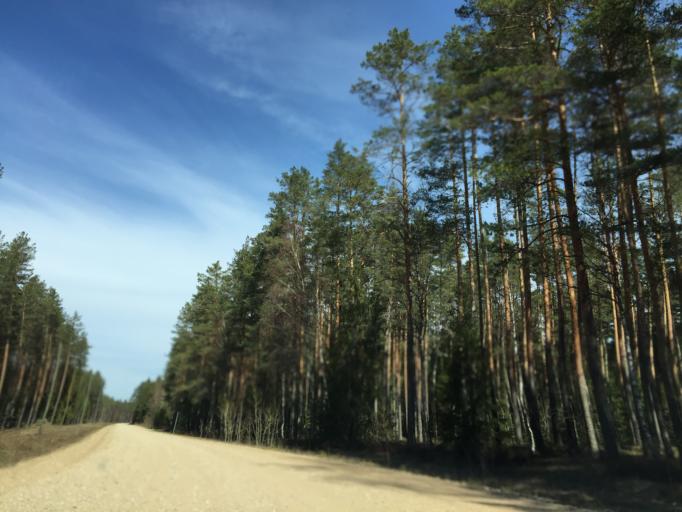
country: LV
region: Strenci
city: Seda
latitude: 57.6335
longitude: 25.8604
